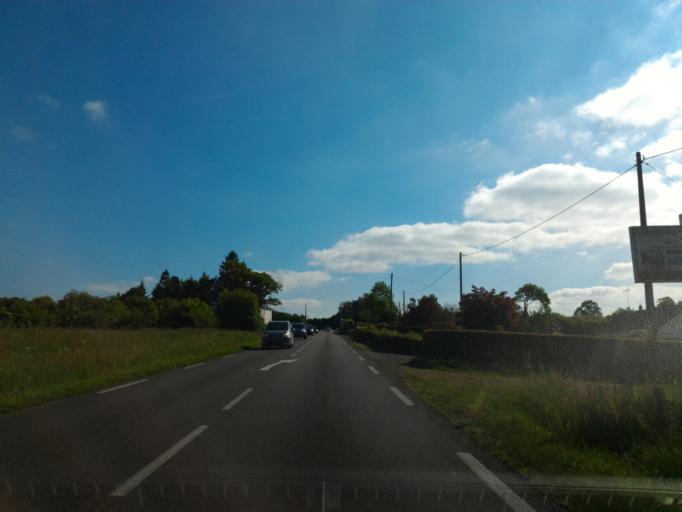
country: FR
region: Lower Normandy
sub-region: Departement de la Manche
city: Villedieu-les-Poeles
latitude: 48.8633
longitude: -1.2048
